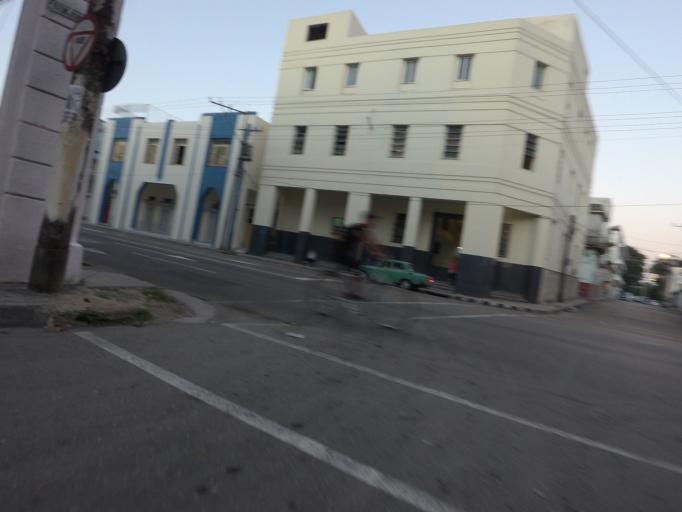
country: CU
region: La Habana
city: Havana
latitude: 23.1267
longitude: -82.3752
